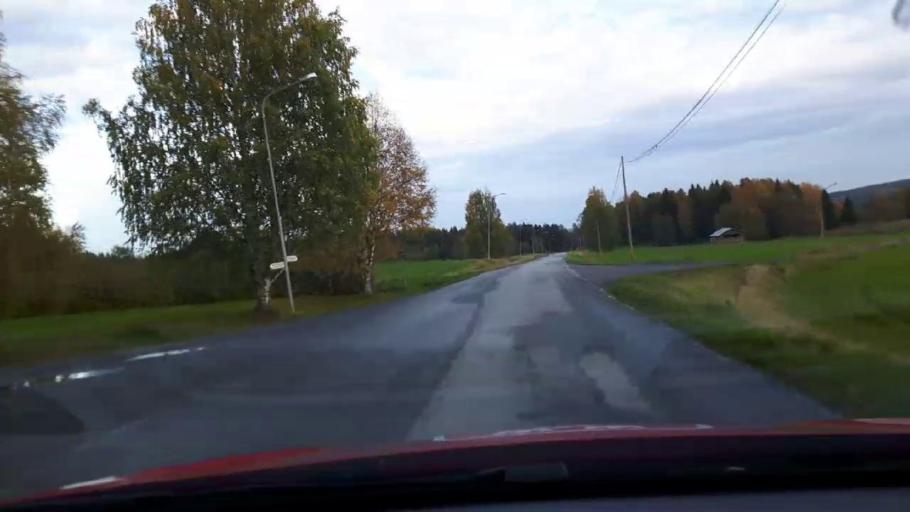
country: SE
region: Jaemtland
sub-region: OEstersunds Kommun
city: Lit
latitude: 63.3224
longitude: 14.8023
